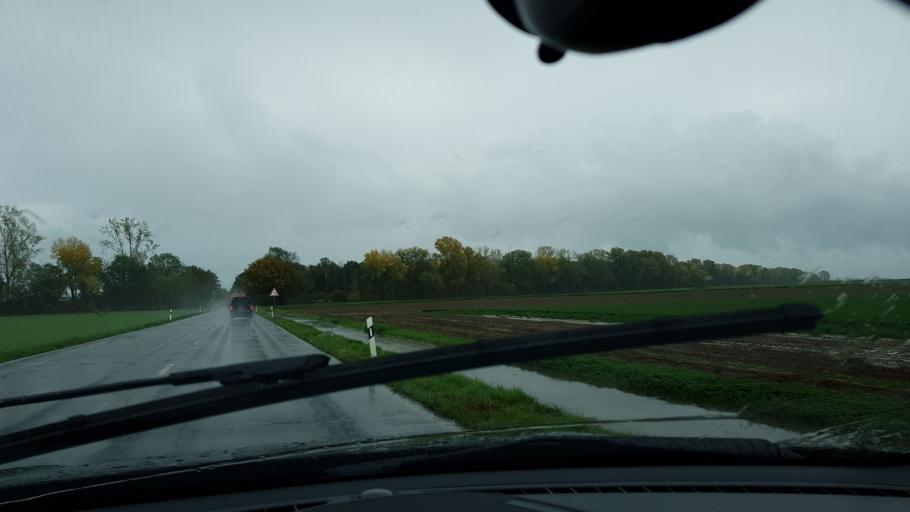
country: DE
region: North Rhine-Westphalia
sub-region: Regierungsbezirk Dusseldorf
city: Rommerskirchen
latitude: 51.0667
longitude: 6.7037
